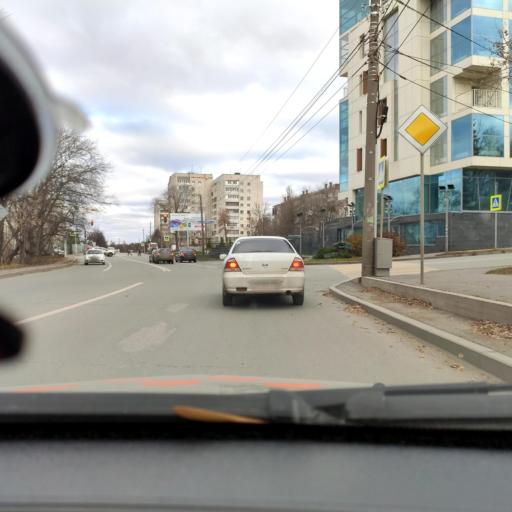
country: RU
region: Bashkortostan
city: Ufa
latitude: 54.7759
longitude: 56.0208
